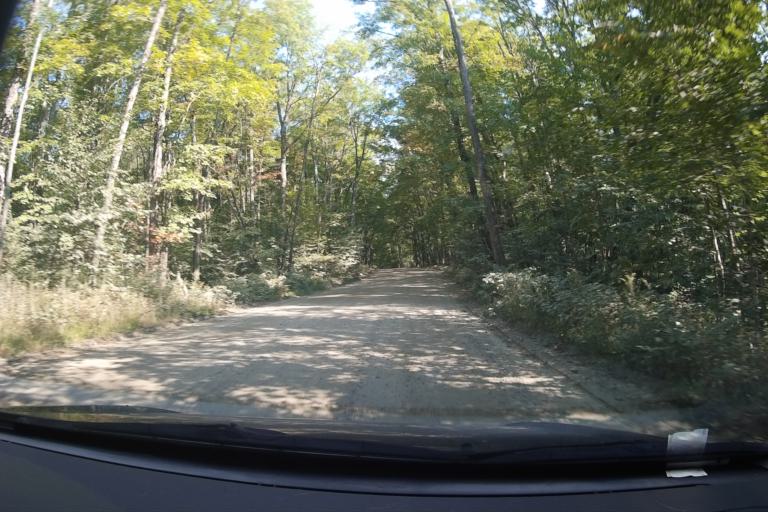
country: CA
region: Ontario
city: Huntsville
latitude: 45.5553
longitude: -78.6959
